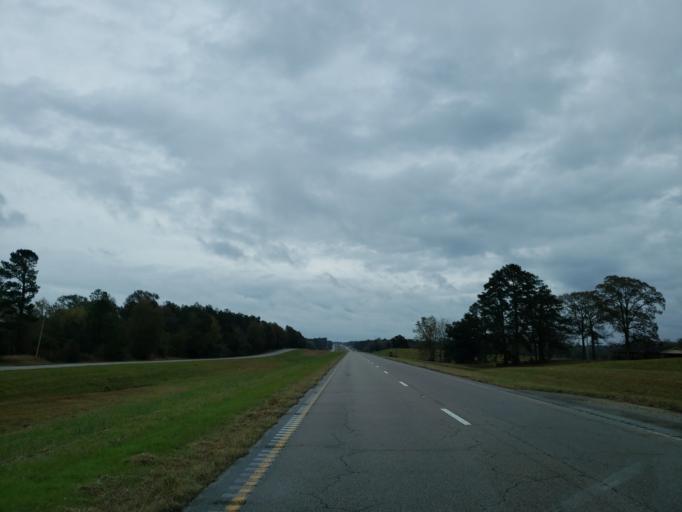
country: US
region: Mississippi
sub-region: Wayne County
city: Waynesboro
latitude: 31.6965
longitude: -88.8587
